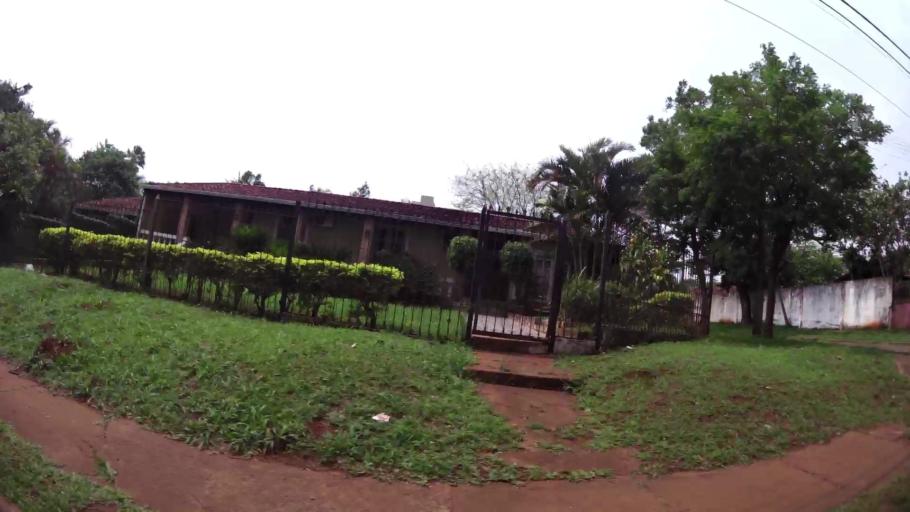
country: PY
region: Alto Parana
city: Presidente Franco
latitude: -25.5521
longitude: -54.6279
